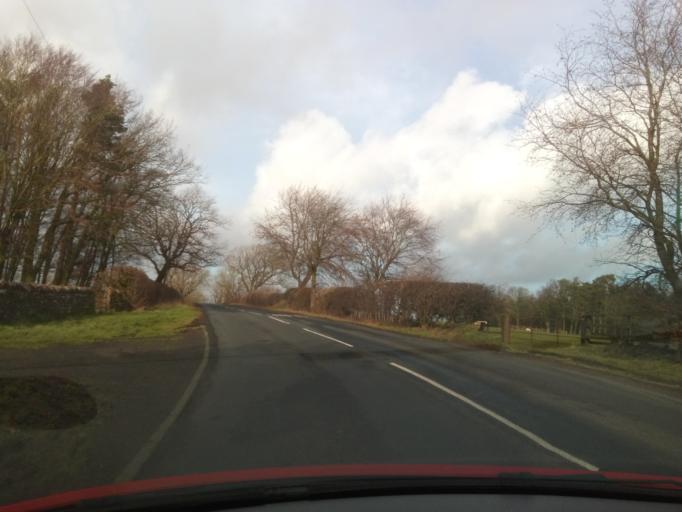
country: GB
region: England
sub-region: Northumberland
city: Rothley
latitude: 55.1108
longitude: -2.0089
